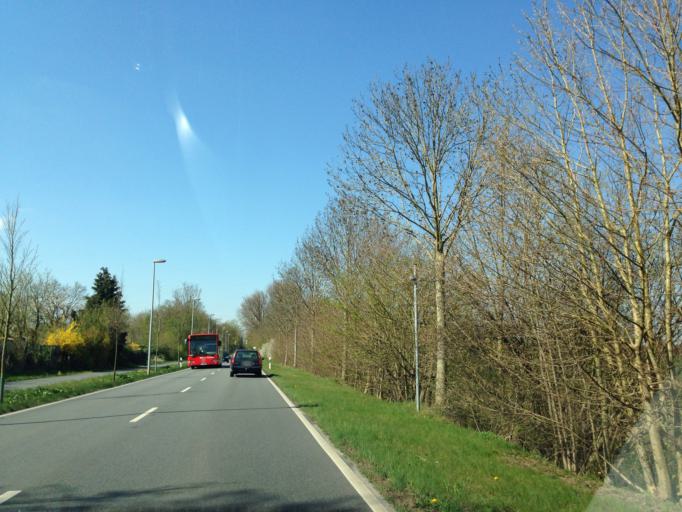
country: DE
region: North Rhine-Westphalia
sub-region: Regierungsbezirk Munster
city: Muenster
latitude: 51.9911
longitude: 7.6237
